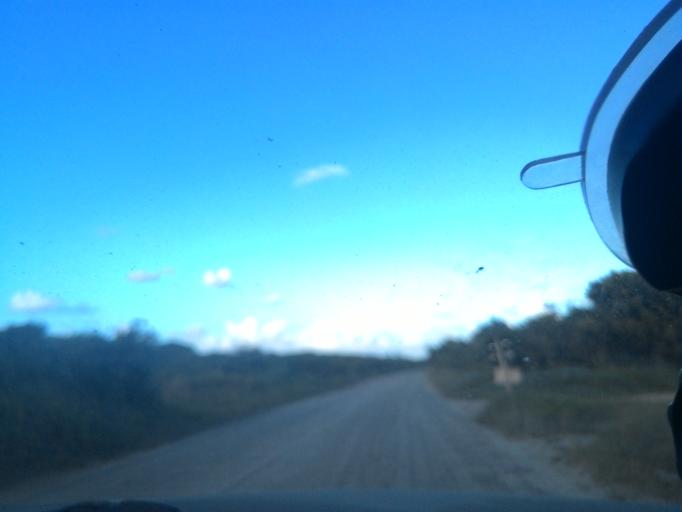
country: BR
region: Sao Paulo
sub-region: Iguape
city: Iguape
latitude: -24.8540
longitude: -47.7027
